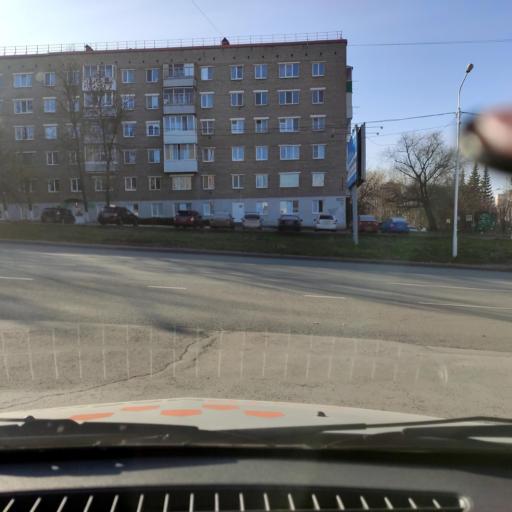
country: RU
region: Bashkortostan
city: Ufa
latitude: 54.7193
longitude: 56.0030
